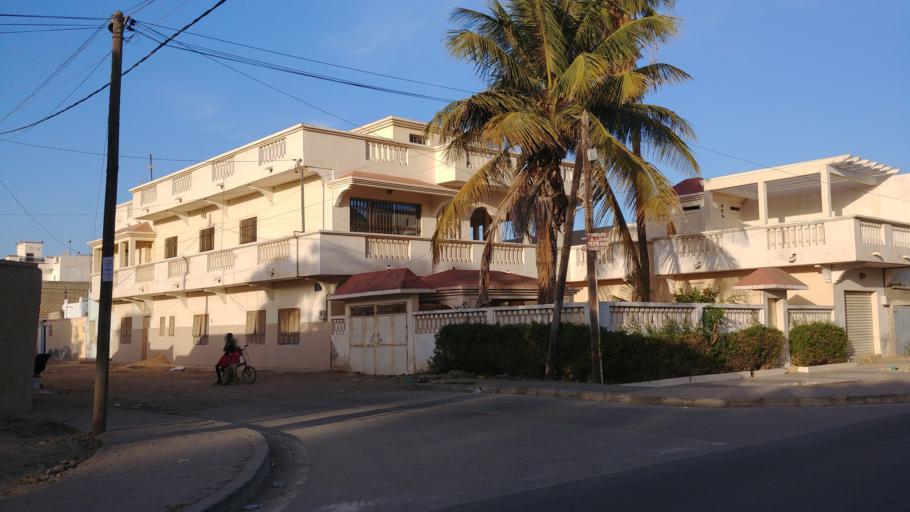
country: SN
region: Saint-Louis
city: Saint-Louis
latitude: 16.0260
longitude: -16.4839
